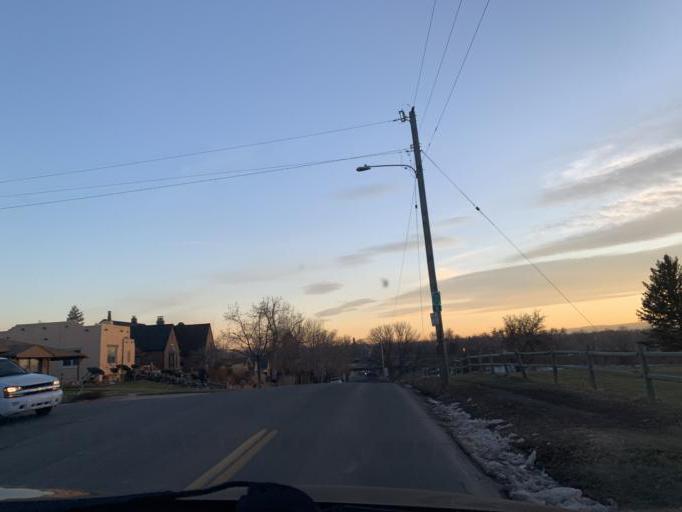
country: US
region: Colorado
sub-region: Adams County
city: Berkley
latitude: 39.7858
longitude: -105.0440
